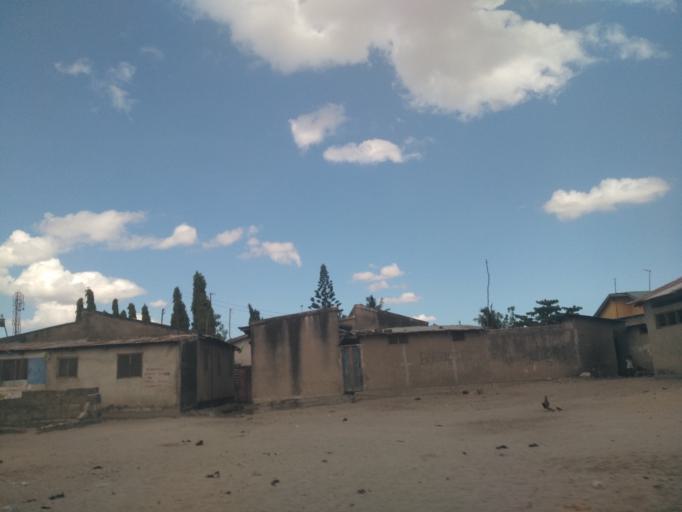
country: TZ
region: Dar es Salaam
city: Dar es Salaam
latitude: -6.8722
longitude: 39.2336
